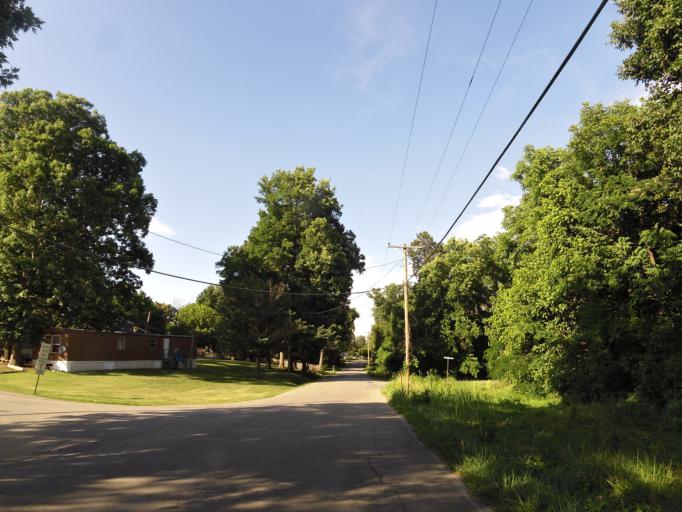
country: US
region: Tennessee
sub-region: Blount County
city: Alcoa
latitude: 35.8194
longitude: -83.9596
